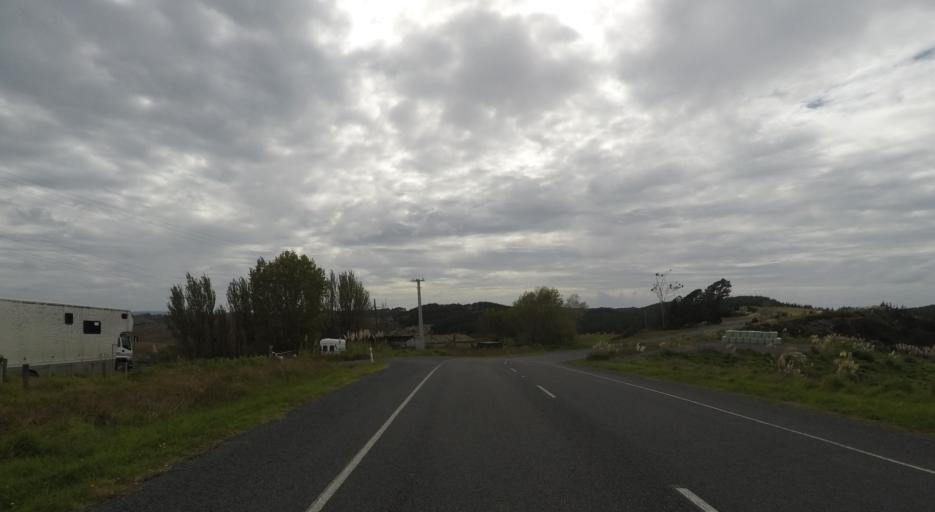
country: NZ
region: Auckland
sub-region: Auckland
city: Rothesay Bay
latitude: -36.6546
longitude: 174.6889
